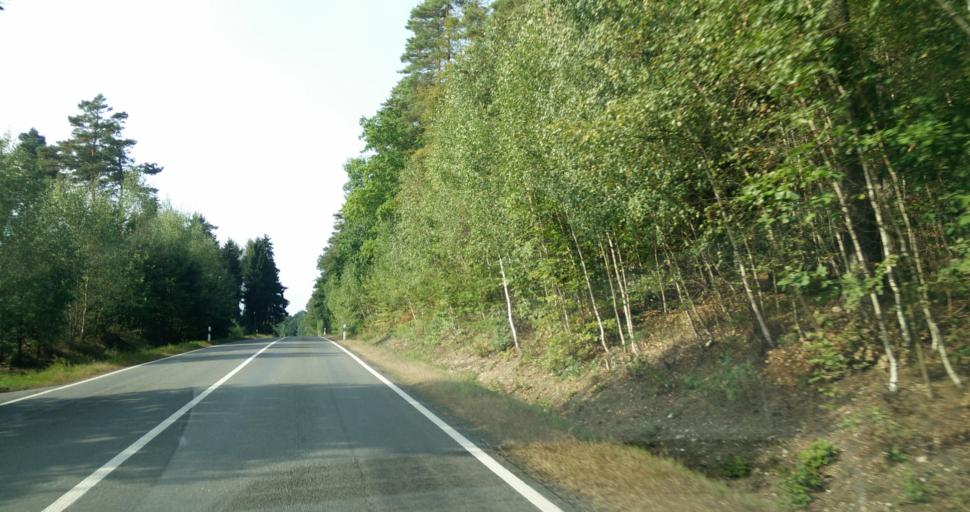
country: DE
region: Saxony
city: Colditz
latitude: 51.1354
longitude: 12.7530
